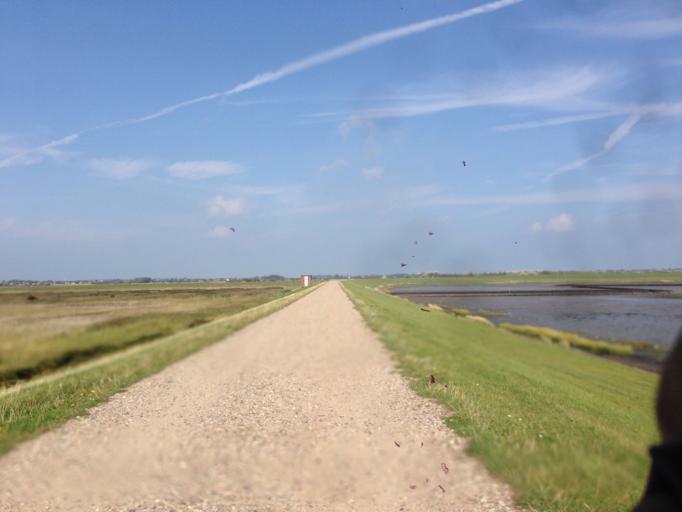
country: DE
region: Schleswig-Holstein
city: Tinnum
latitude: 54.8775
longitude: 8.3363
